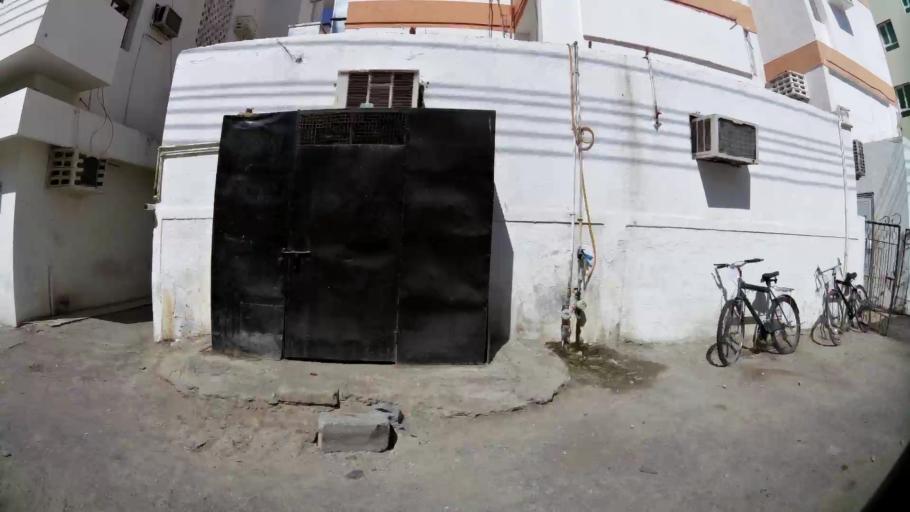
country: OM
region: Muhafazat Masqat
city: Muscat
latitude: 23.5958
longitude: 58.5447
